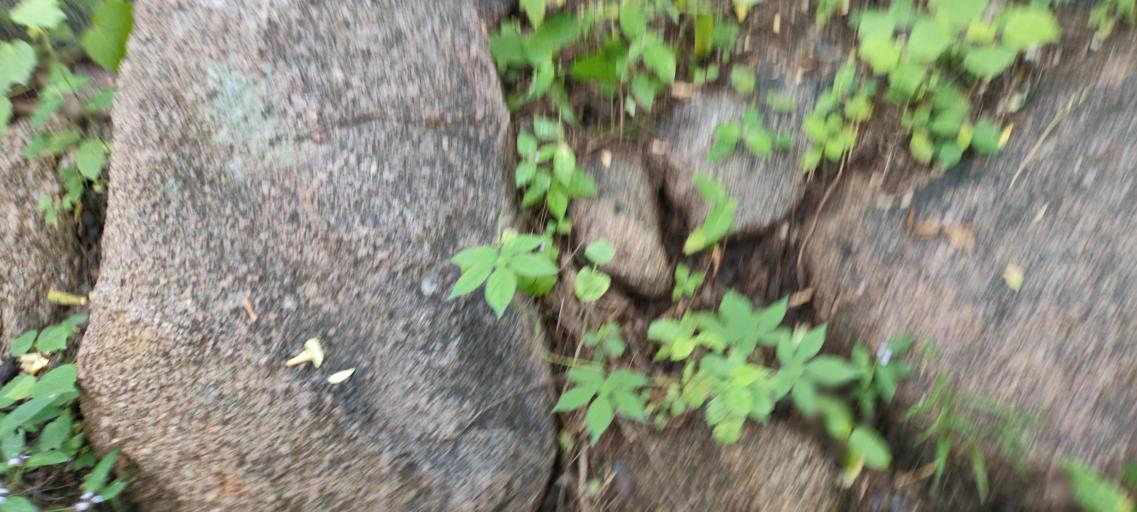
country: IN
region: Telangana
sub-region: Mahbubnagar
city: Farrukhnagar
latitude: 16.8948
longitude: 78.4952
